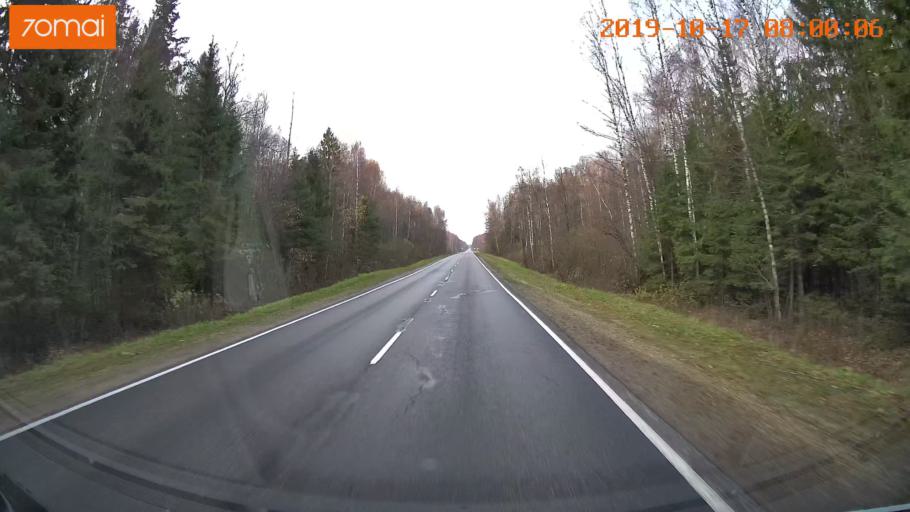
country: RU
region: Vladimir
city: Bavleny
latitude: 56.3870
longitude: 39.5245
